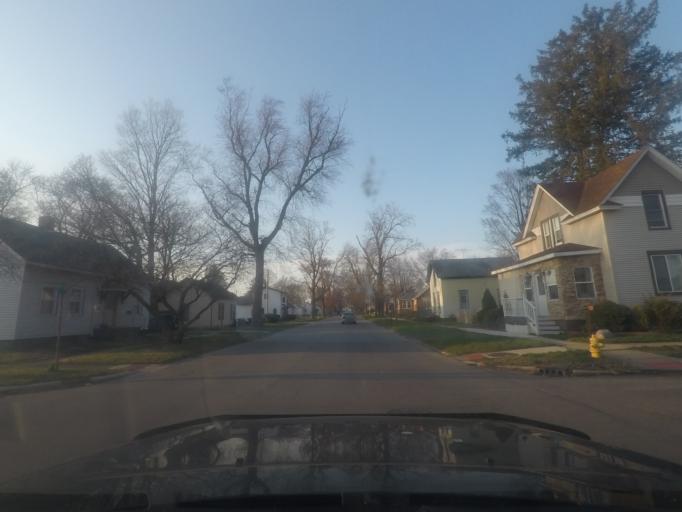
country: US
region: Indiana
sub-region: LaPorte County
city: LaPorte
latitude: 41.6029
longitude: -86.7291
